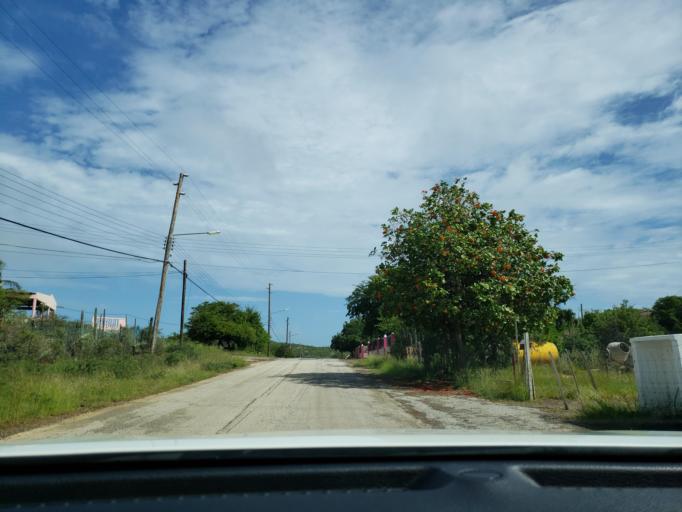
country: CW
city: Barber
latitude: 12.3031
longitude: -69.0929
